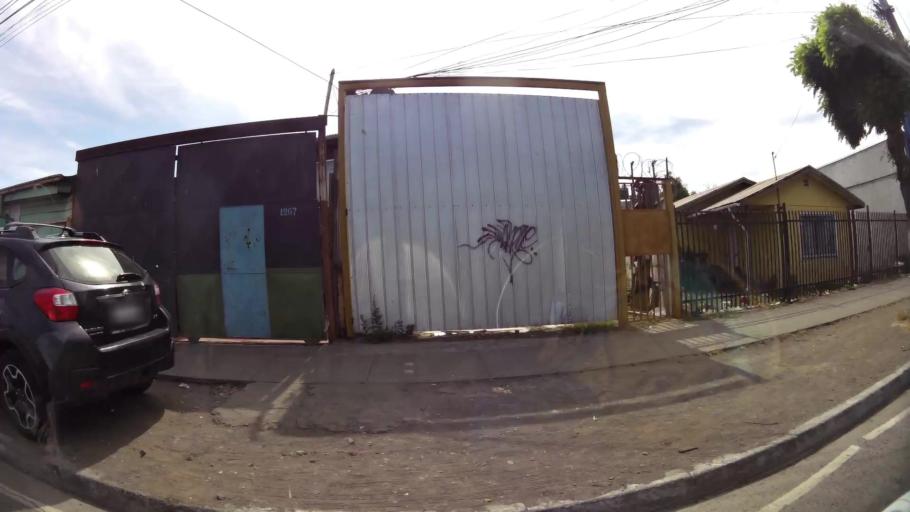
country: CL
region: Biobio
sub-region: Provincia de Concepcion
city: Talcahuano
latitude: -36.7245
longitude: -73.1172
